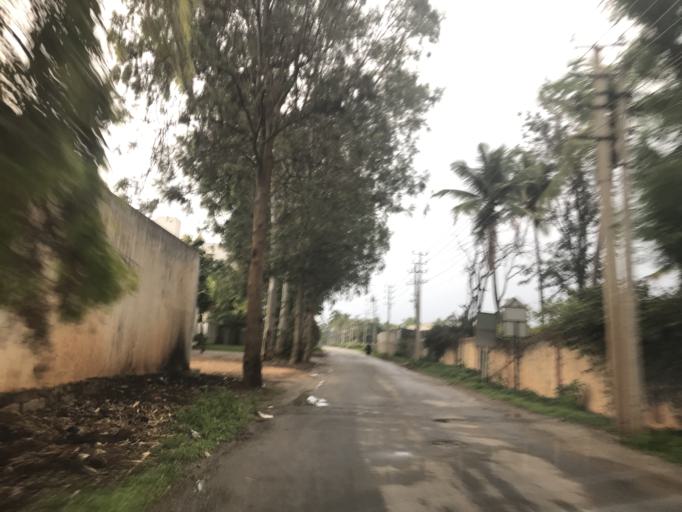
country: IN
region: Karnataka
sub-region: Bangalore Rural
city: Devanhalli
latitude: 13.1882
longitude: 77.6520
